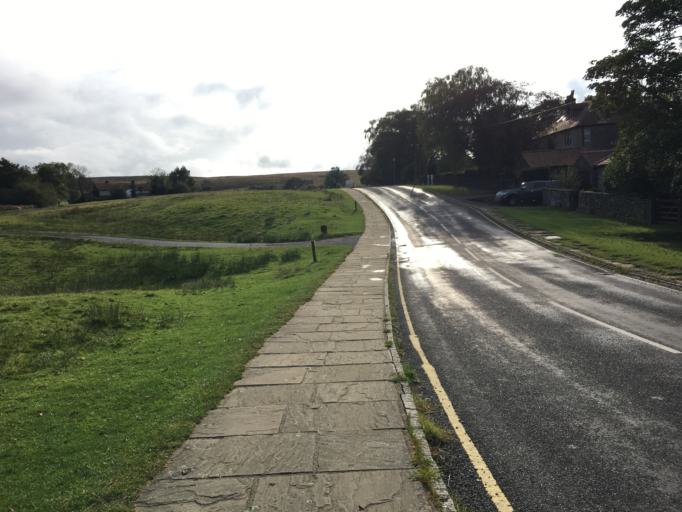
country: GB
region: England
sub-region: North Yorkshire
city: Sleights
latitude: 54.3973
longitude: -0.7231
